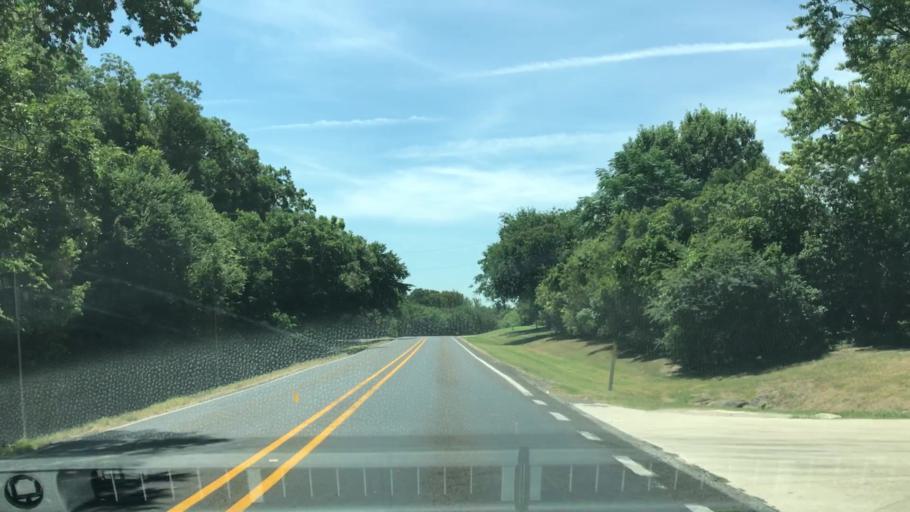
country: US
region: Texas
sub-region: Collin County
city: Fairview
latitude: 33.1460
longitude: -96.6066
